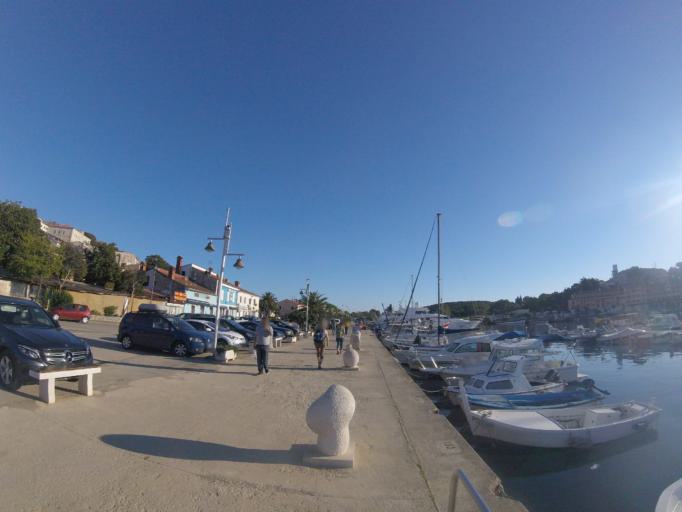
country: HR
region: Istarska
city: Vrsar
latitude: 45.1502
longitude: 13.6026
